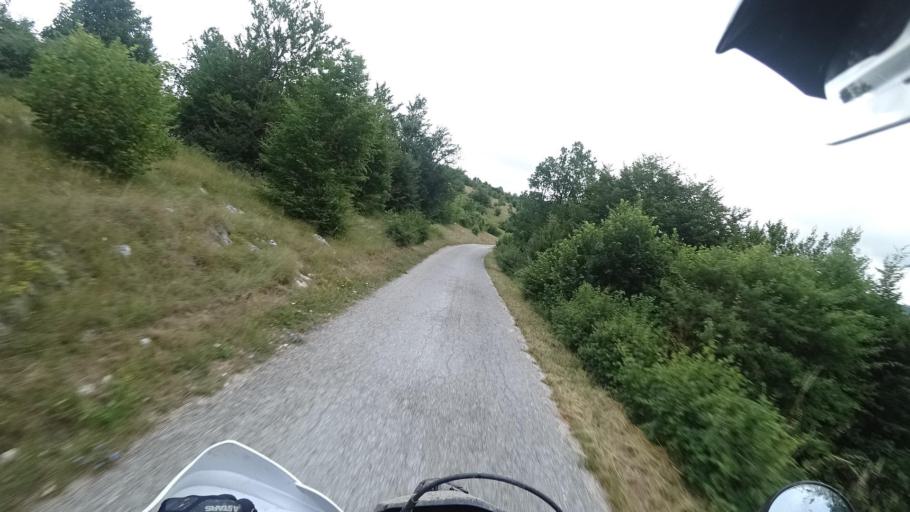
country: HR
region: Licko-Senjska
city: Jezerce
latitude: 44.7512
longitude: 15.4805
